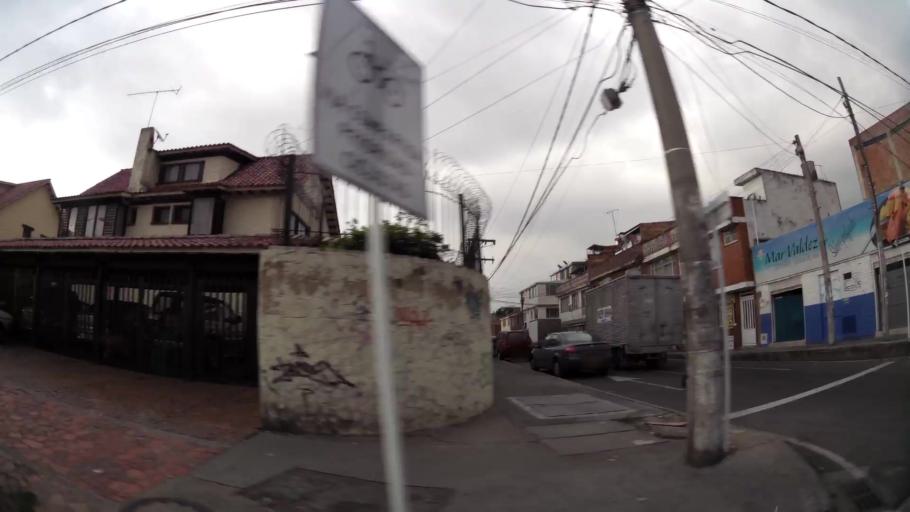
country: CO
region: Bogota D.C.
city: Barrio San Luis
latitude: 4.7185
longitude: -74.0698
